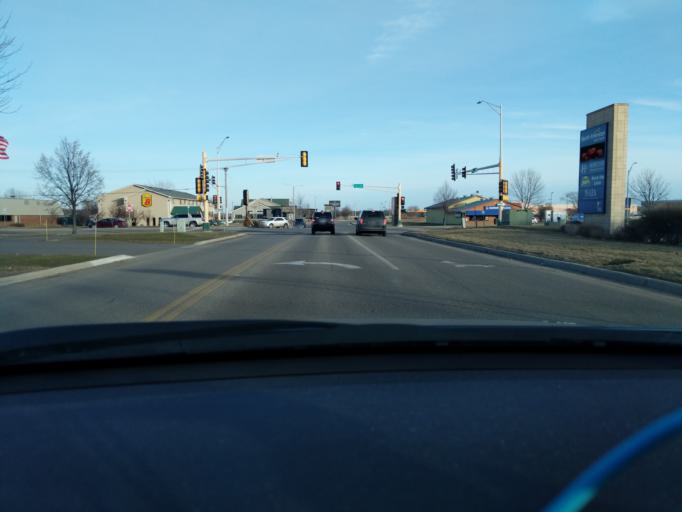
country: US
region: Minnesota
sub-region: Kandiyohi County
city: Willmar
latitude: 45.0961
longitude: -95.0434
